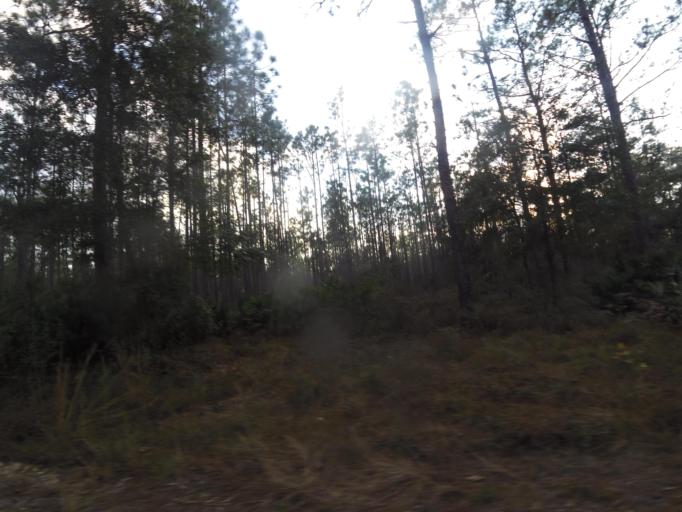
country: US
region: Florida
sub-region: Clay County
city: Middleburg
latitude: 30.1310
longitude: -81.9441
